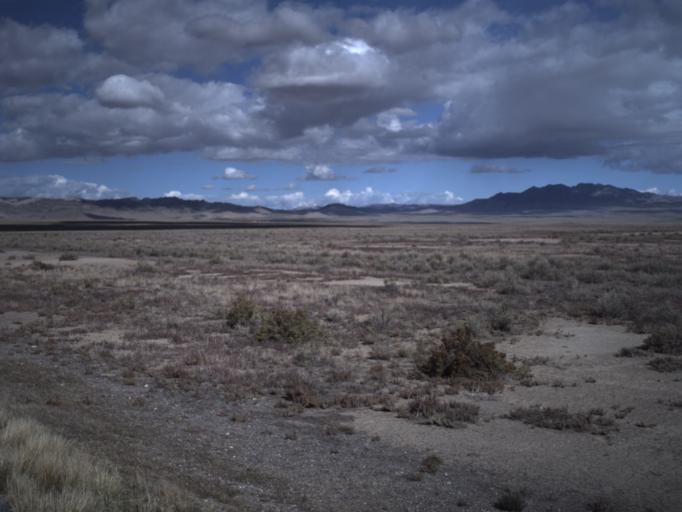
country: US
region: Utah
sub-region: Beaver County
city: Milford
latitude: 38.5414
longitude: -113.7064
